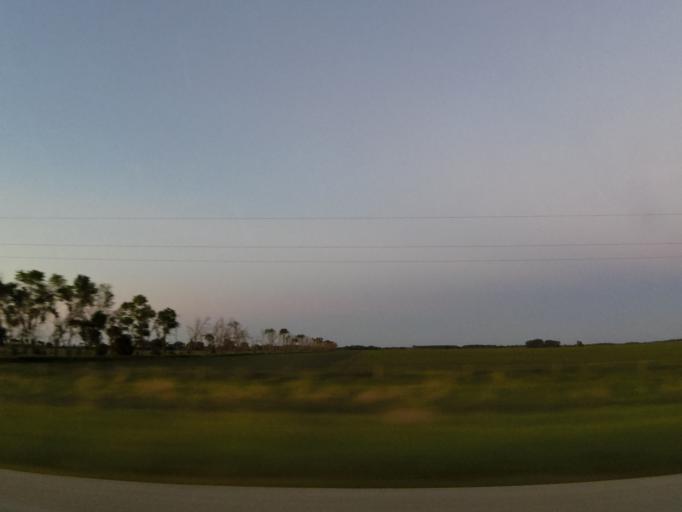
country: US
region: North Dakota
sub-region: Walsh County
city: Grafton
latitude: 48.3897
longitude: -97.1900
